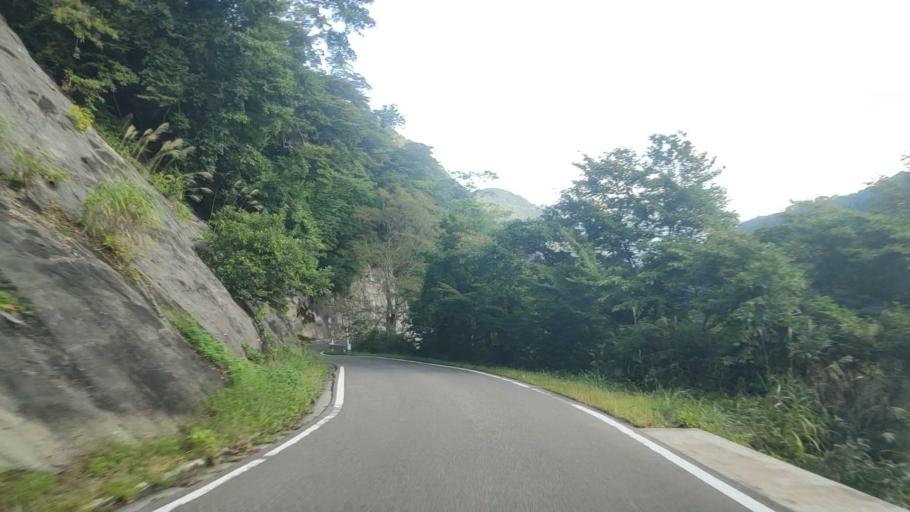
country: JP
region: Toyama
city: Yatsuomachi-higashikumisaka
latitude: 36.4993
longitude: 137.0488
